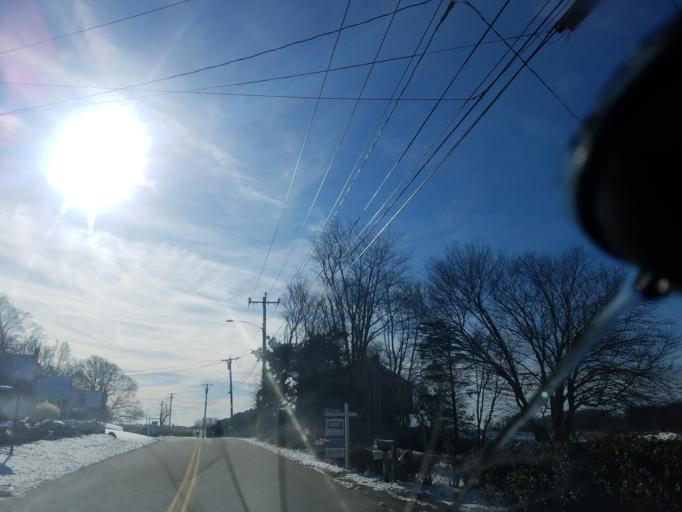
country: US
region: Connecticut
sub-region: New London County
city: Niantic
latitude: 41.3078
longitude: -72.2176
